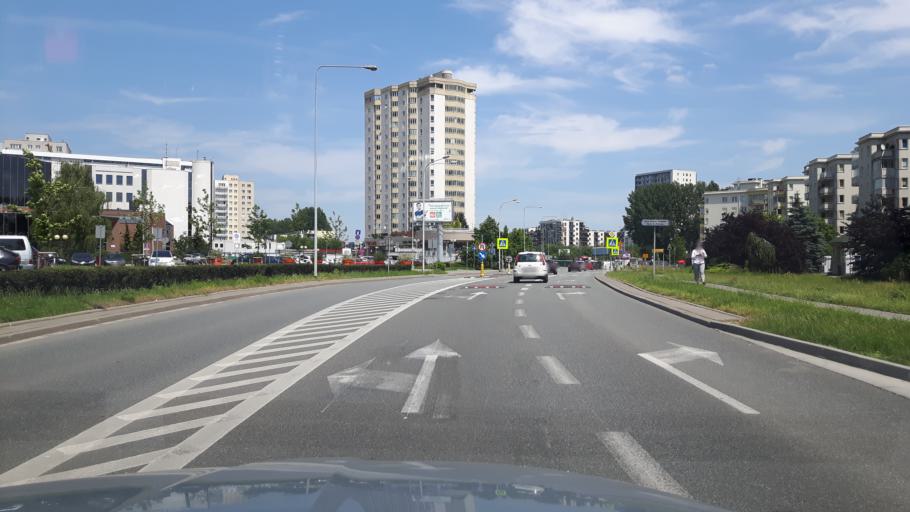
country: PL
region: Masovian Voivodeship
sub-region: Warszawa
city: Targowek
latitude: 52.2900
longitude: 21.0492
